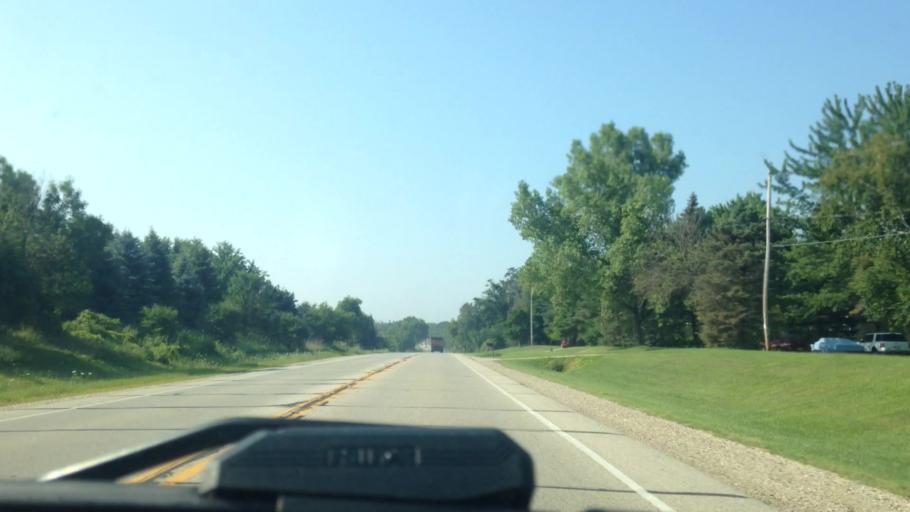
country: US
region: Wisconsin
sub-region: Waukesha County
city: Merton
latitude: 43.1892
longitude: -88.2617
